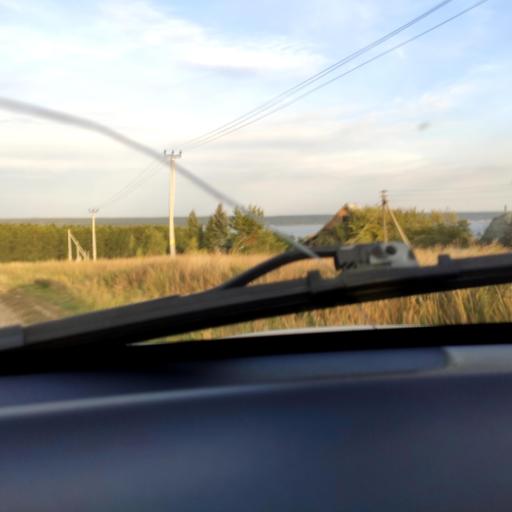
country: RU
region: Tatarstan
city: Verkhniy Uslon
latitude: 55.6537
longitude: 48.9485
